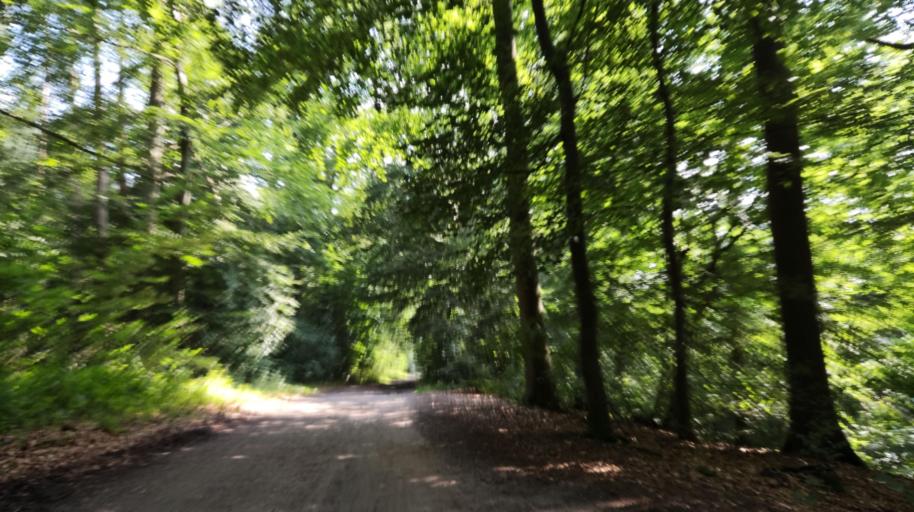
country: DE
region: Lower Saxony
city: Deutsch Evern
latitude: 53.2230
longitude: 10.4233
